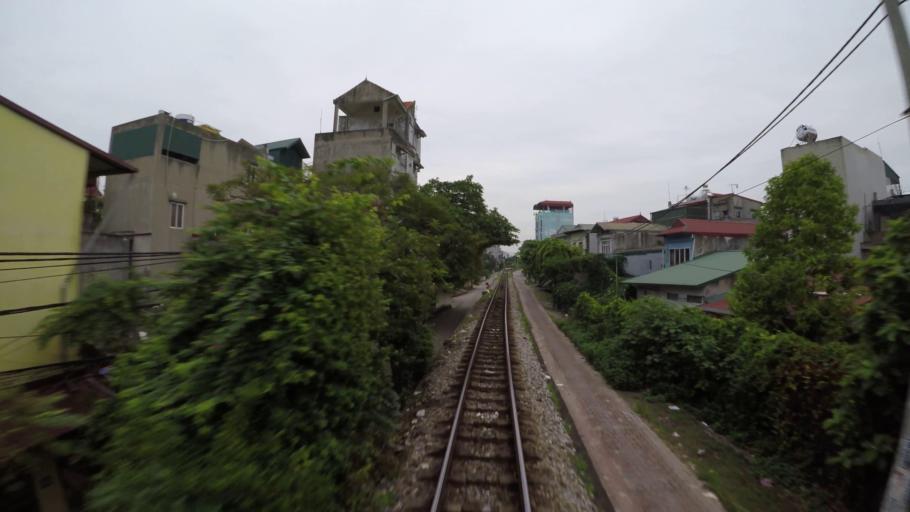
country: VN
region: Ha Noi
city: Trau Quy
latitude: 21.0212
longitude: 105.9371
